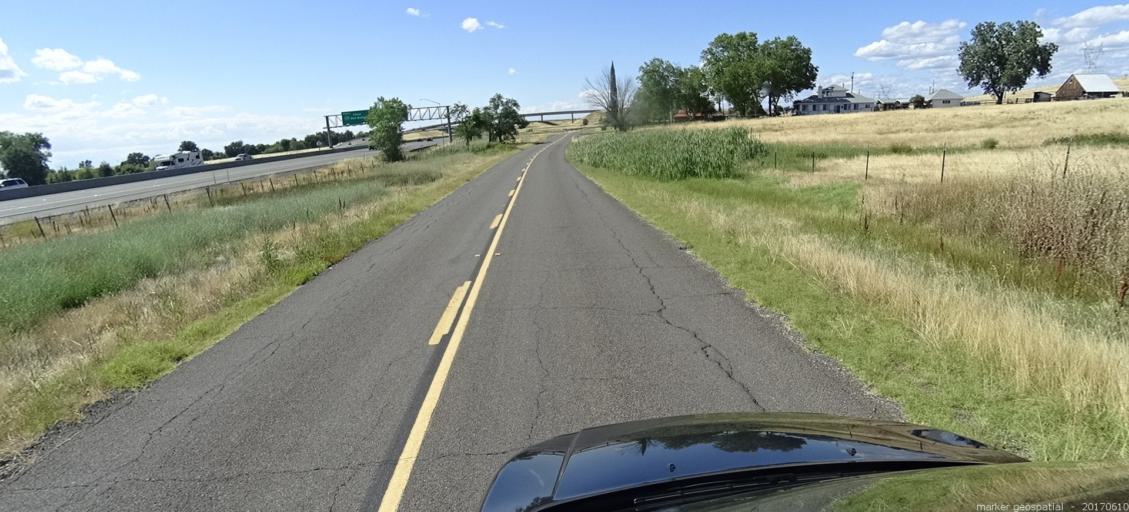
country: US
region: California
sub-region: Butte County
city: Thermalito
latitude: 39.5776
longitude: -121.6180
